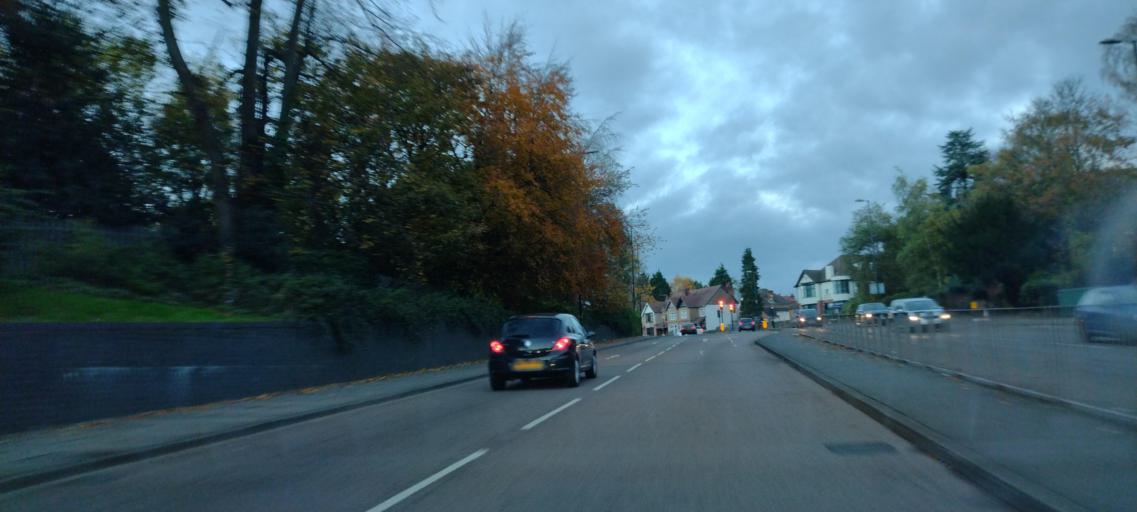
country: GB
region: England
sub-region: Coventry
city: Coventry
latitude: 52.4136
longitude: -1.5150
